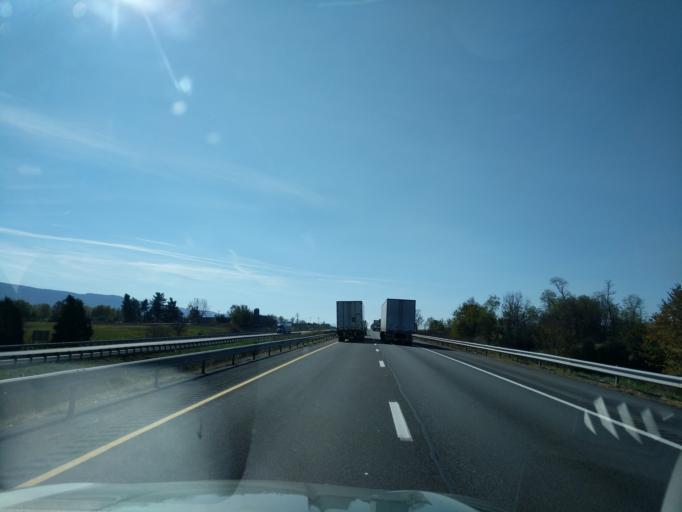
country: US
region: Virginia
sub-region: Shenandoah County
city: New Market
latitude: 38.6747
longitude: -78.6620
